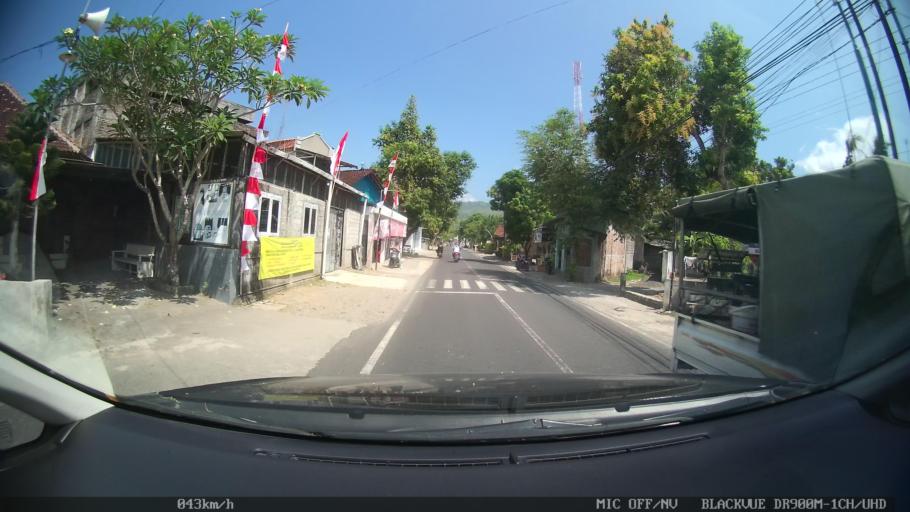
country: ID
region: Daerah Istimewa Yogyakarta
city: Pundong
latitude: -7.9421
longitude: 110.3743
